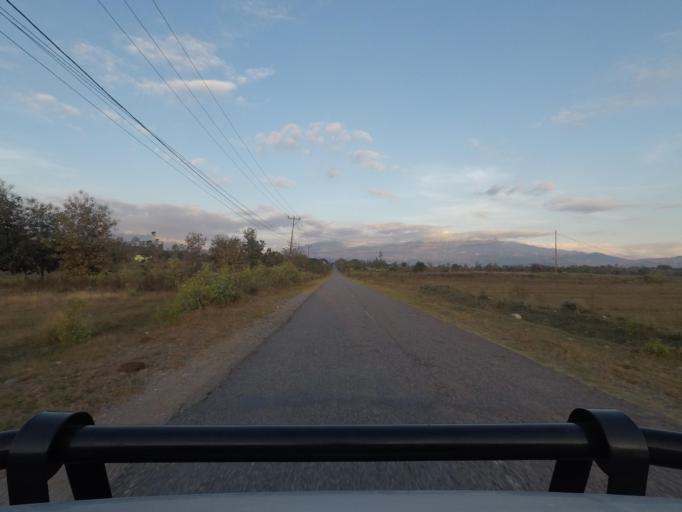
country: TL
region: Bobonaro
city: Maliana
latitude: -8.9704
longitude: 125.1326
